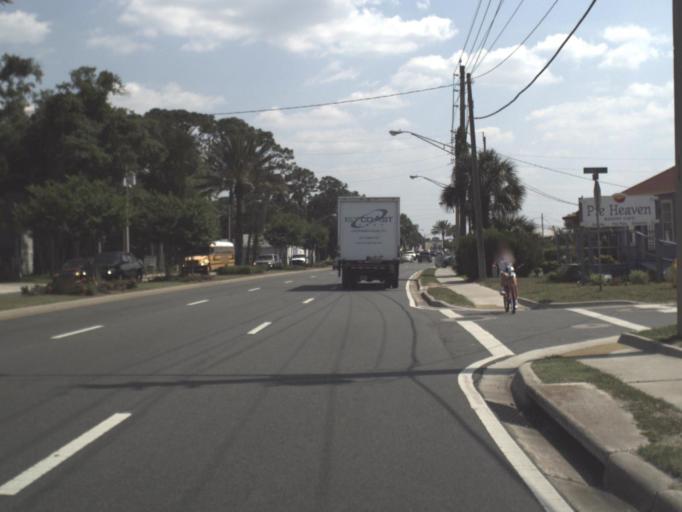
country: US
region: Florida
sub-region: Duval County
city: Atlantic Beach
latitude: 30.3393
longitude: -81.4135
